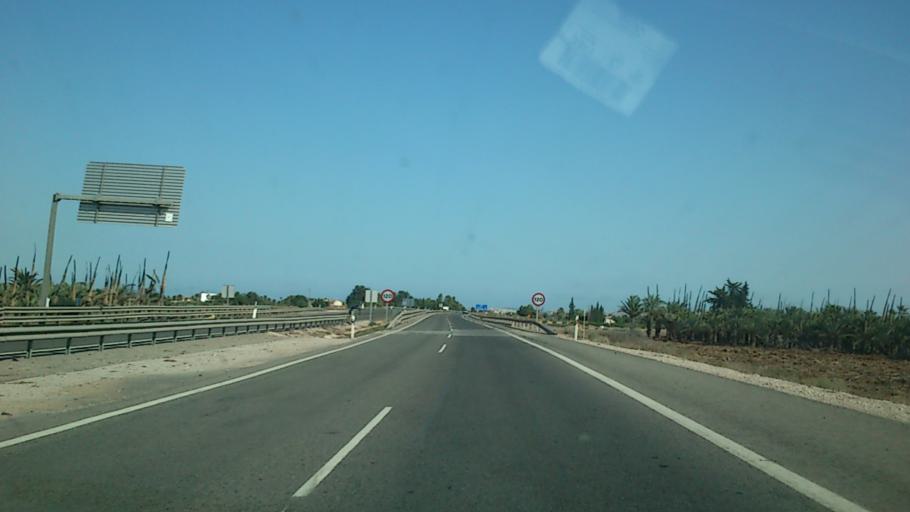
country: ES
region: Valencia
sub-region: Provincia de Alicante
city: Catral
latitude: 38.1443
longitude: -0.8154
